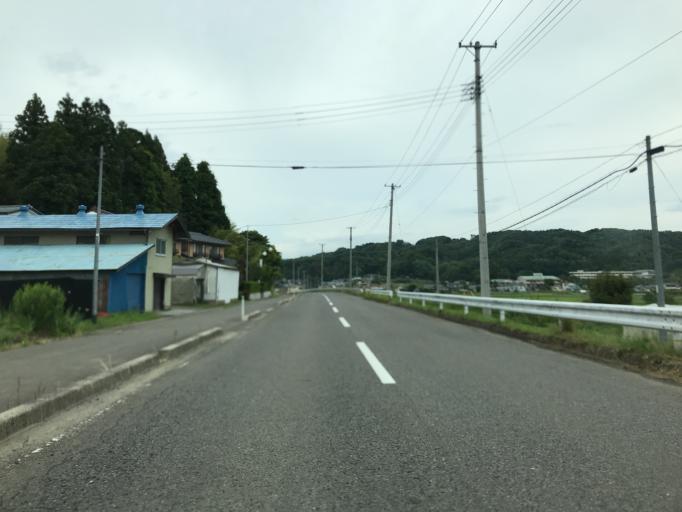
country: JP
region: Fukushima
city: Funehikimachi-funehiki
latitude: 37.3933
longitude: 140.5643
